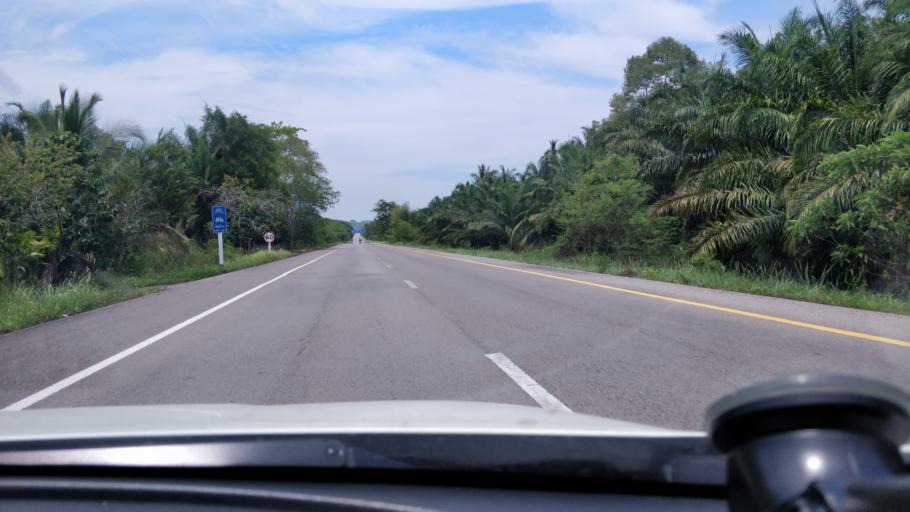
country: TH
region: Krabi
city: Plai Phraya
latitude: 8.5667
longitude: 98.9241
